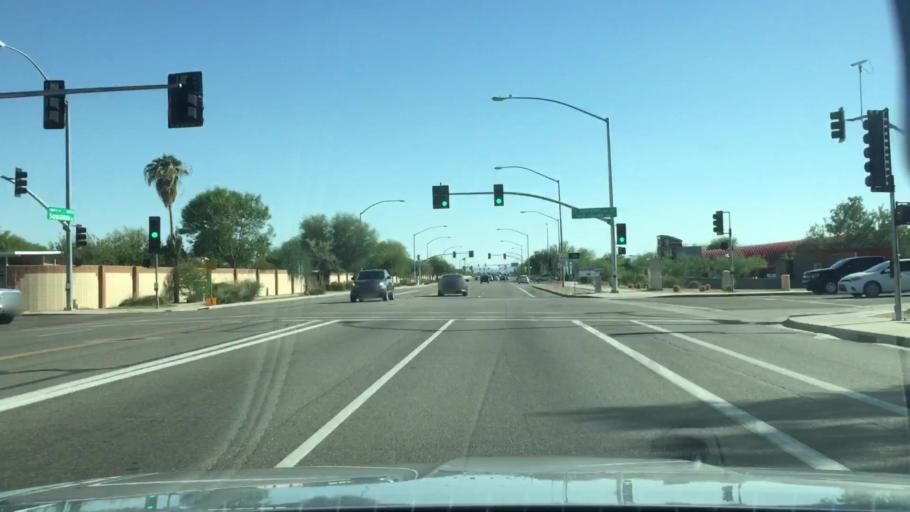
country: US
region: Arizona
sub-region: Pinal County
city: Apache Junction
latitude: 33.3918
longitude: -111.6676
